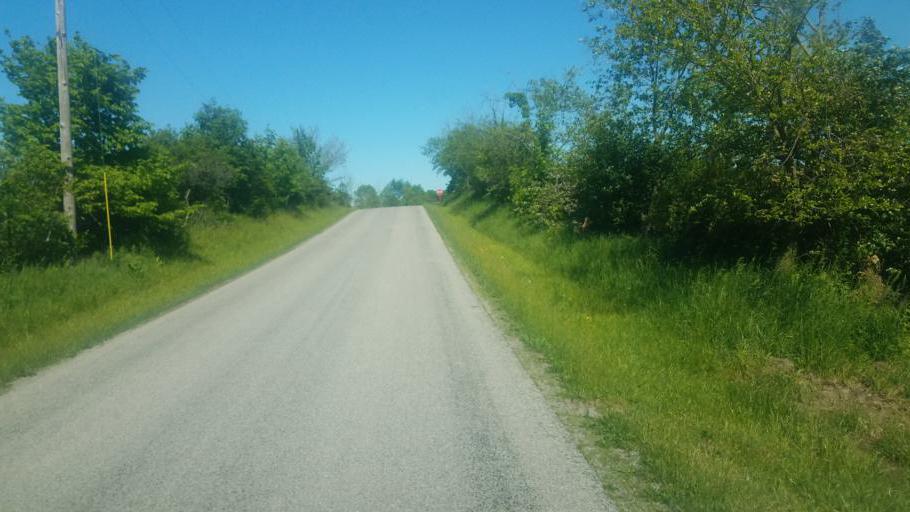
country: US
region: Ohio
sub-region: Logan County
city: Northwood
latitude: 40.4378
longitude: -83.7180
